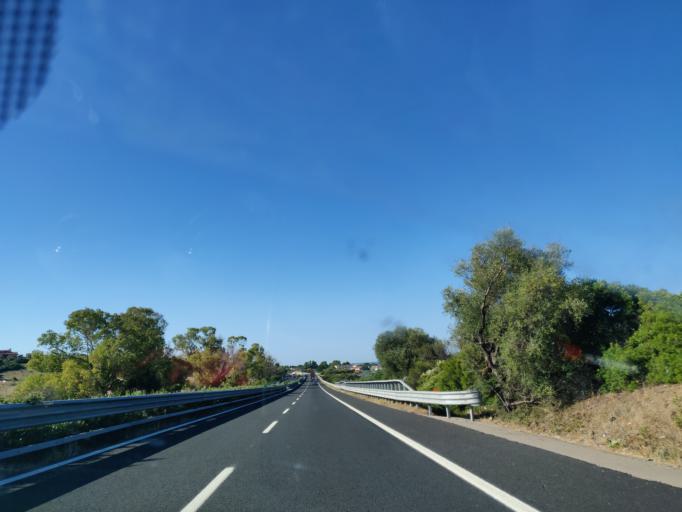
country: IT
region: Latium
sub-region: Citta metropolitana di Roma Capitale
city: Civitavecchia
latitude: 42.0713
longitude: 11.8230
